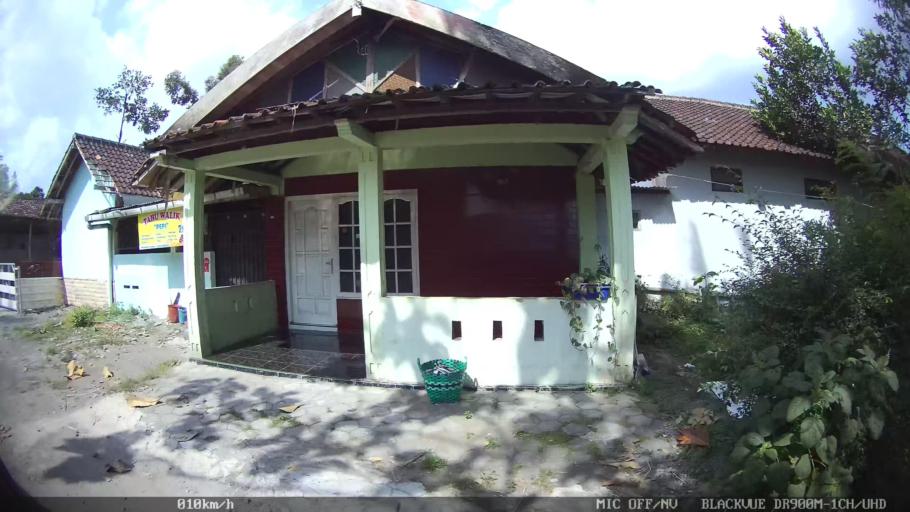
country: ID
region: Daerah Istimewa Yogyakarta
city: Kasihan
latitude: -7.8138
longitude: 110.3306
